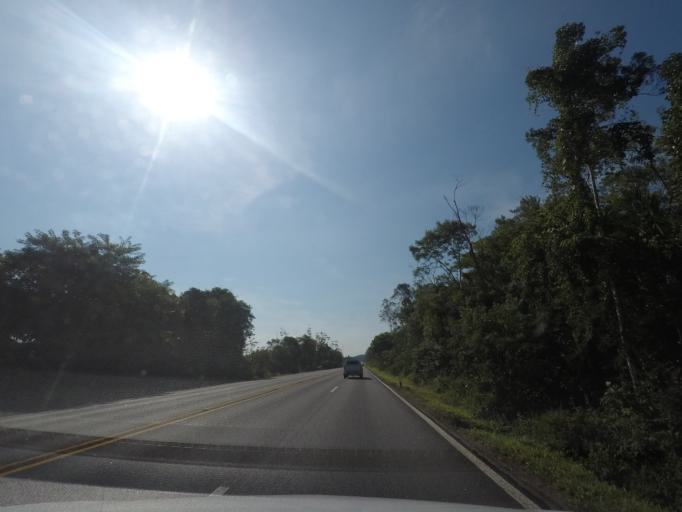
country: BR
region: Parana
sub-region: Paranagua
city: Paranagua
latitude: -25.5882
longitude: -48.6115
